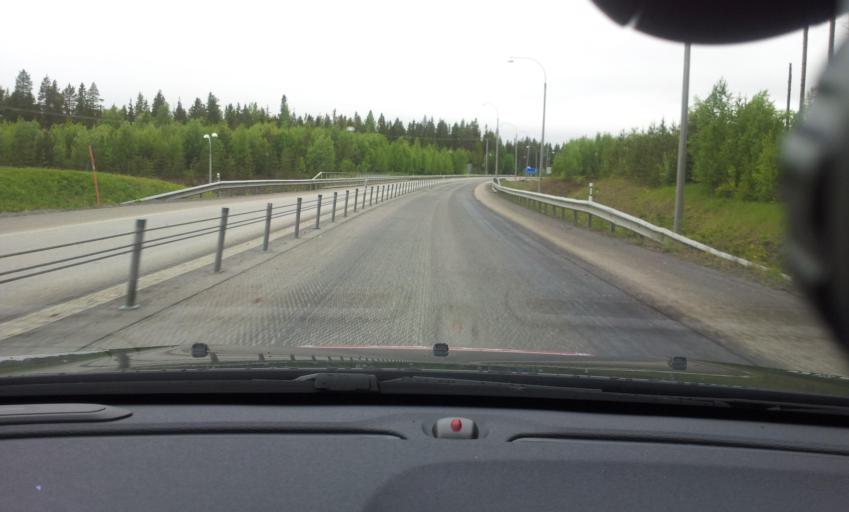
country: SE
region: Jaemtland
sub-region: OEstersunds Kommun
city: Ostersund
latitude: 63.2159
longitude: 14.6364
